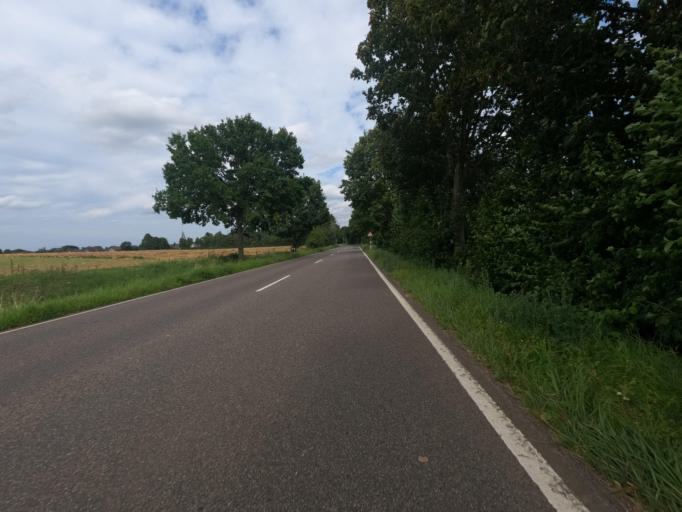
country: DE
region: North Rhine-Westphalia
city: Geilenkirchen
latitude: 50.9865
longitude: 6.1773
